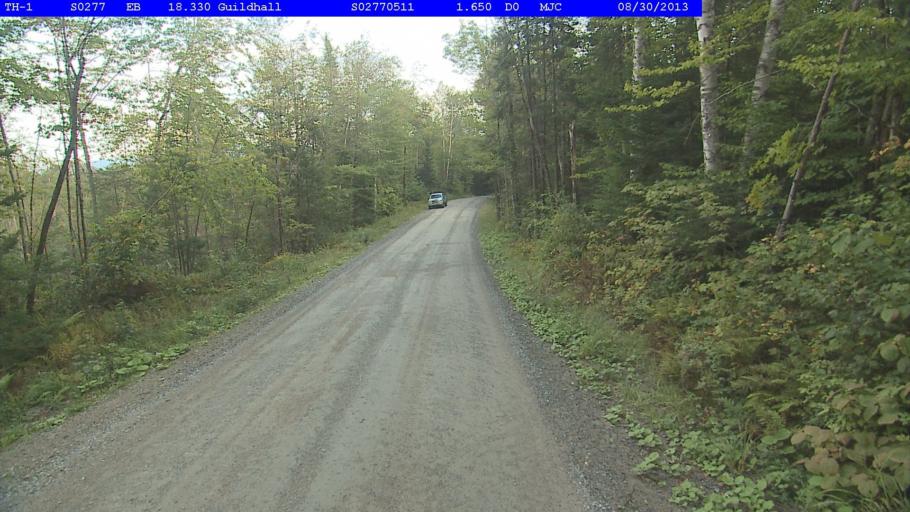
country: US
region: Vermont
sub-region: Essex County
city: Guildhall
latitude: 44.5639
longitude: -71.6414
